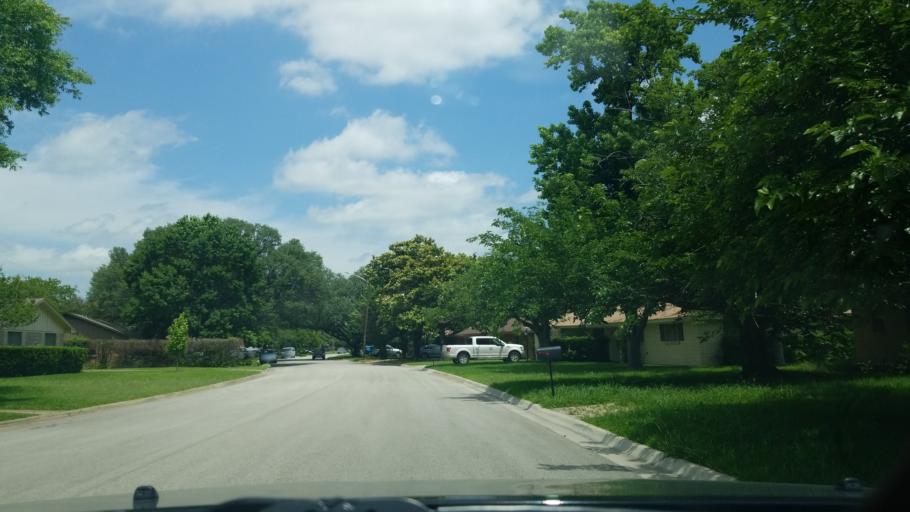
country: US
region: Texas
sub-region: Denton County
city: Denton
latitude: 33.2253
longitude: -97.1598
